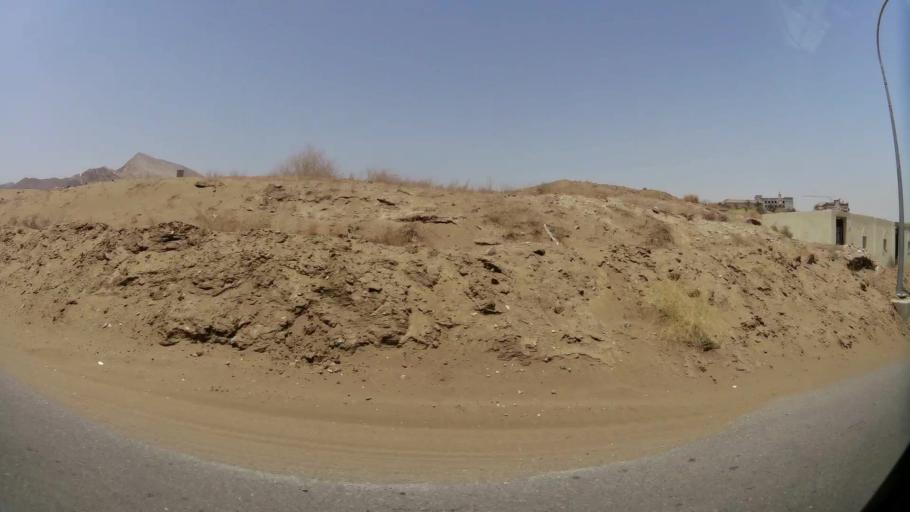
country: OM
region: Muhafazat Masqat
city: Bawshar
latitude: 23.5759
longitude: 58.4252
